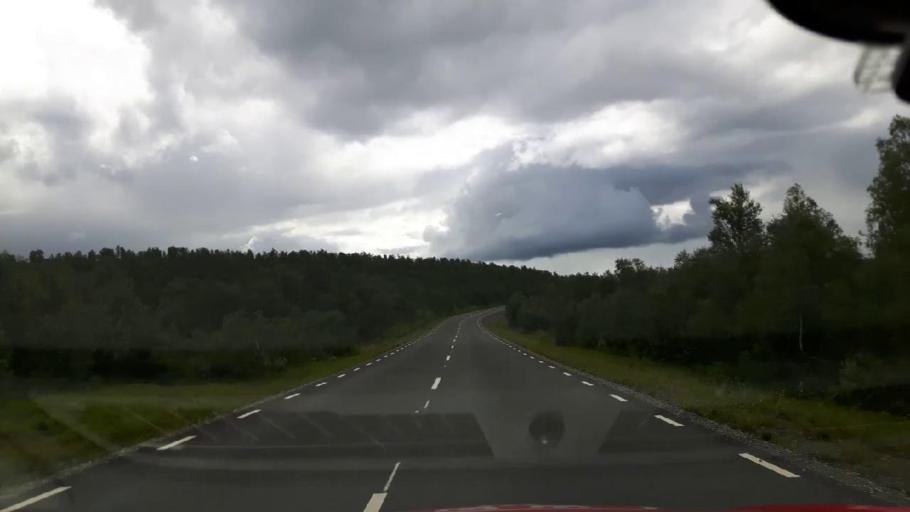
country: NO
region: Nord-Trondelag
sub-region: Royrvik
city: Royrvik
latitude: 64.9762
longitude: 14.2129
